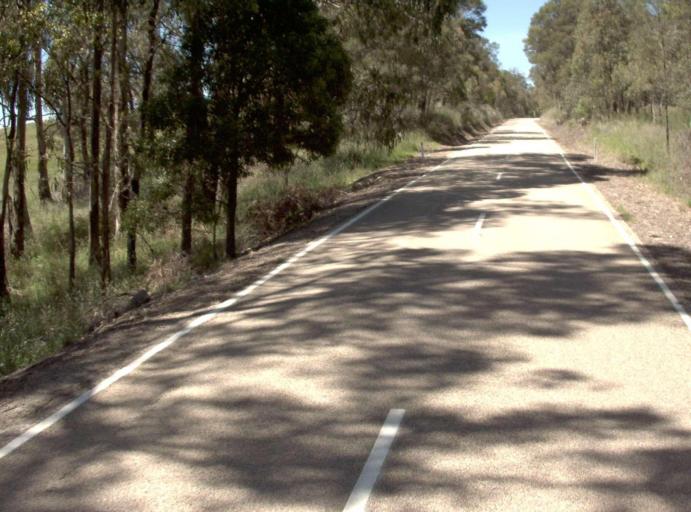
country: AU
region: Victoria
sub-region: East Gippsland
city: Lakes Entrance
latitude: -37.2707
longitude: 148.2558
